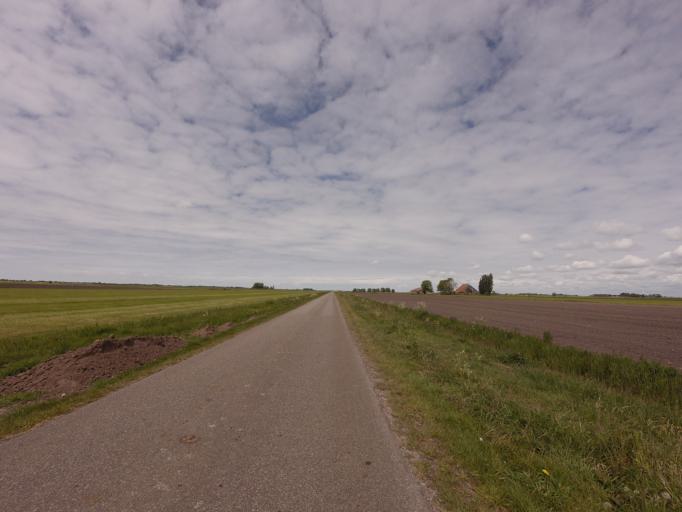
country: NL
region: Friesland
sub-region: Gemeente Gaasterlan-Sleat
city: Oudemirdum
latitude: 52.9002
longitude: 5.5093
